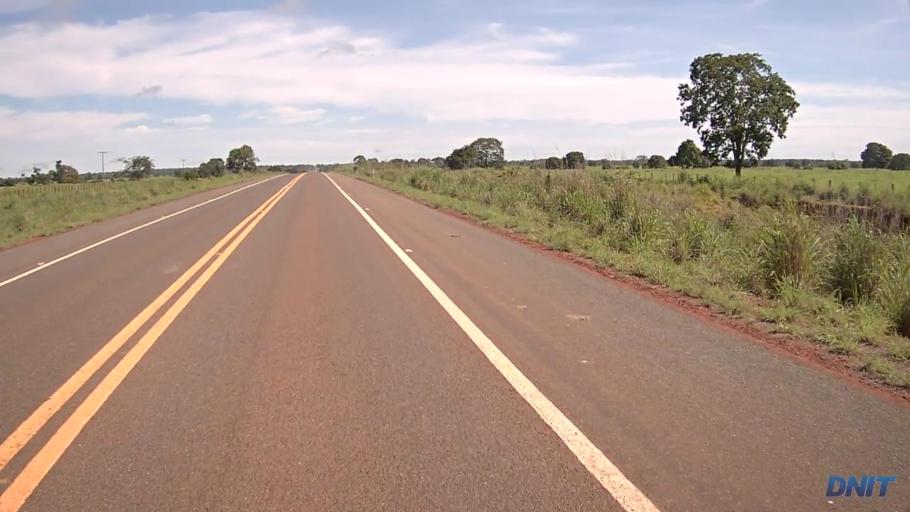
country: BR
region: Goias
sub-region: Sao Miguel Do Araguaia
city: Sao Miguel do Araguaia
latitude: -13.3715
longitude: -50.1435
